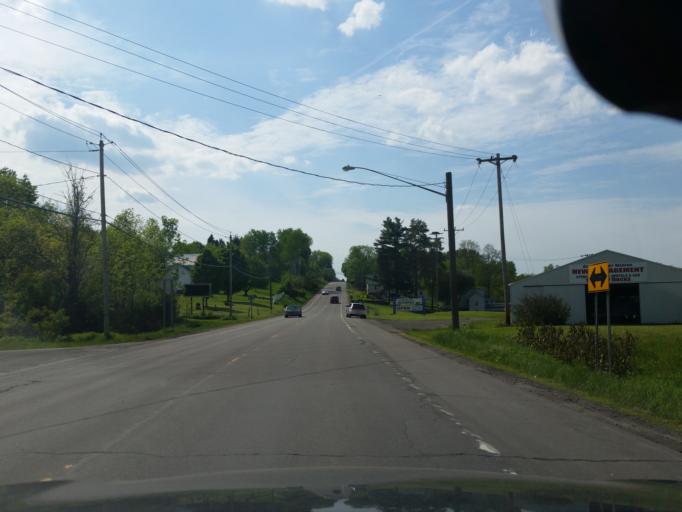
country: US
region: New York
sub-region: Chautauqua County
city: Lakewood
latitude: 42.1062
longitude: -79.3703
